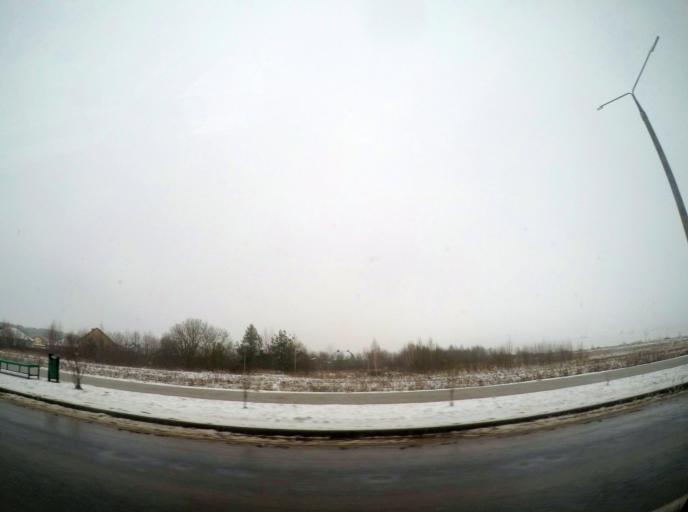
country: BY
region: Grodnenskaya
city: Hrodna
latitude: 53.6122
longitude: 23.8209
